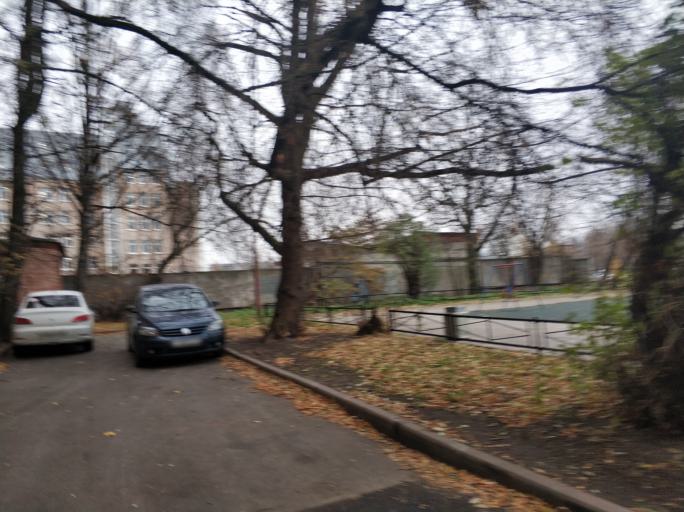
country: RU
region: Leningrad
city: Sampsonievskiy
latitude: 59.9705
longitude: 30.3447
